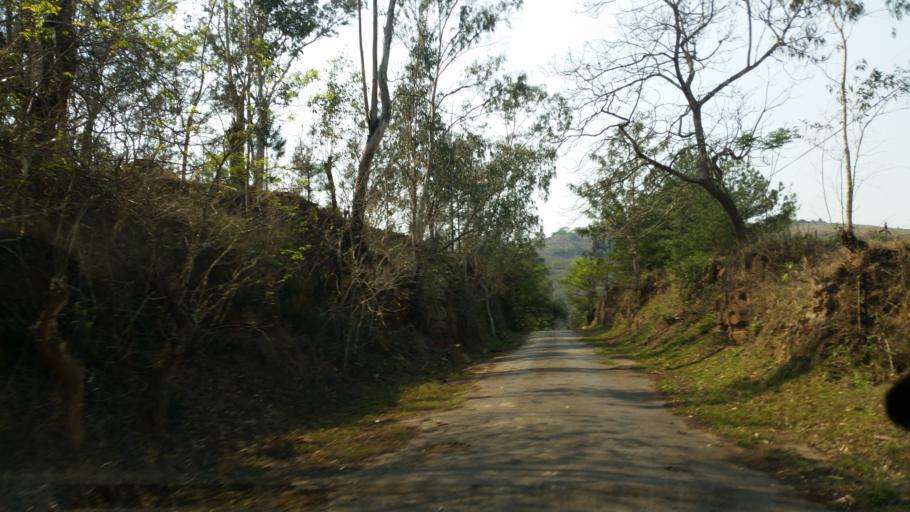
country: ZA
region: KwaZulu-Natal
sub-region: eThekwini Metropolitan Municipality
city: Mpumalanga
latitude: -29.7421
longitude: 30.6648
